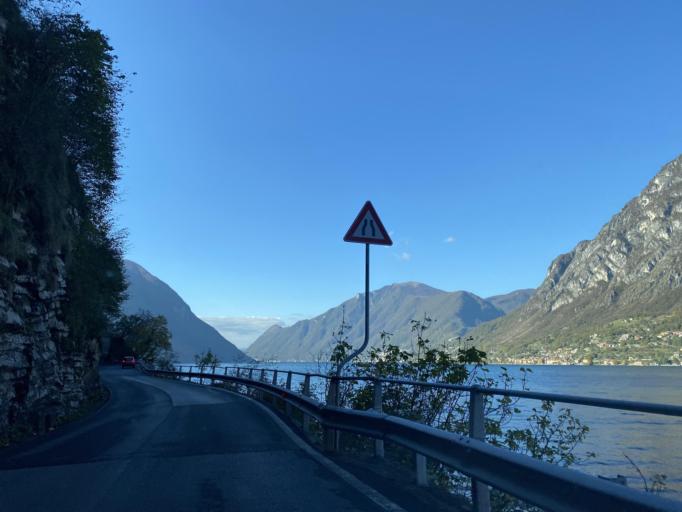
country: IT
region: Lombardy
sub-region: Provincia di Como
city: Porlezza
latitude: 46.0186
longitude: 9.1130
